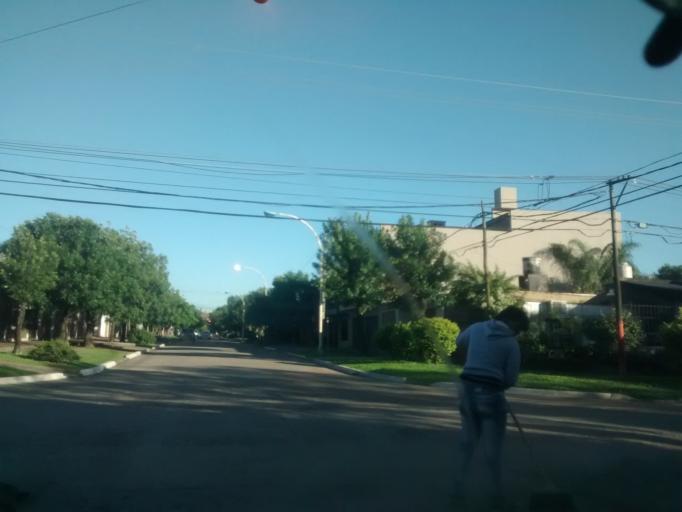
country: AR
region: Chaco
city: Resistencia
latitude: -27.4649
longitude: -58.9962
